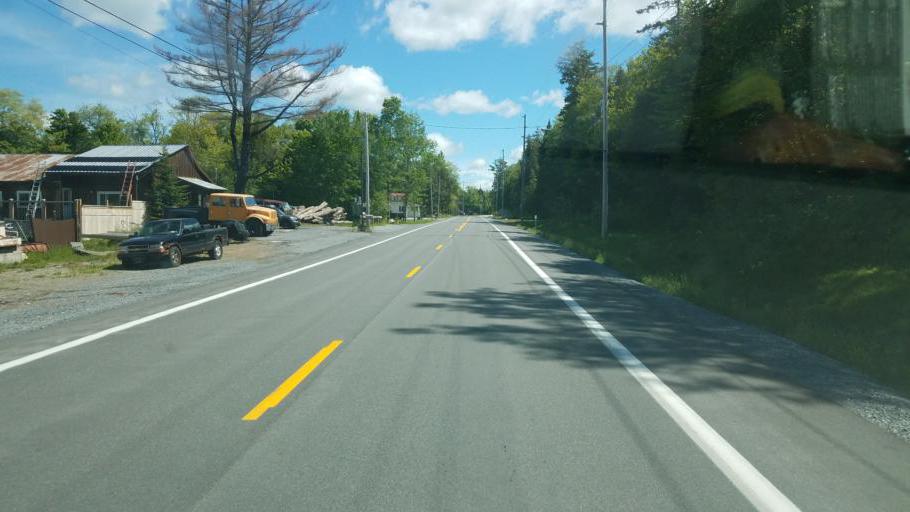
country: US
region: New York
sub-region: Oneida County
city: Boonville
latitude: 43.5840
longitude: -75.1206
